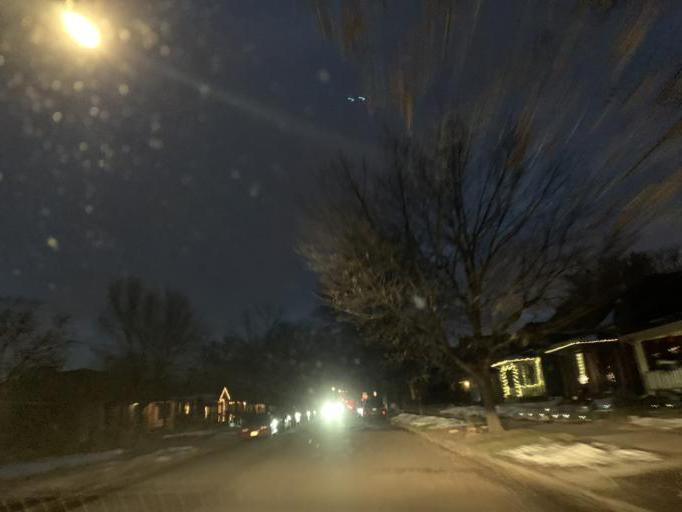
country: US
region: Colorado
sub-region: Jefferson County
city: Edgewater
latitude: 39.7740
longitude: -105.0486
